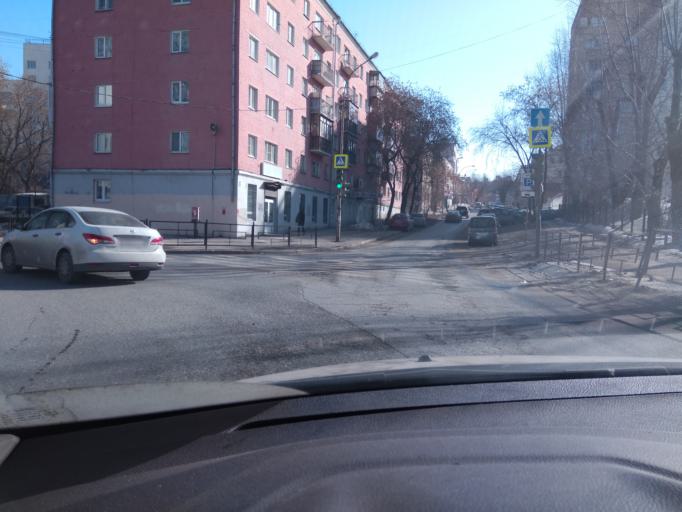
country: RU
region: Sverdlovsk
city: Yekaterinburg
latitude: 56.8419
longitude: 60.5731
